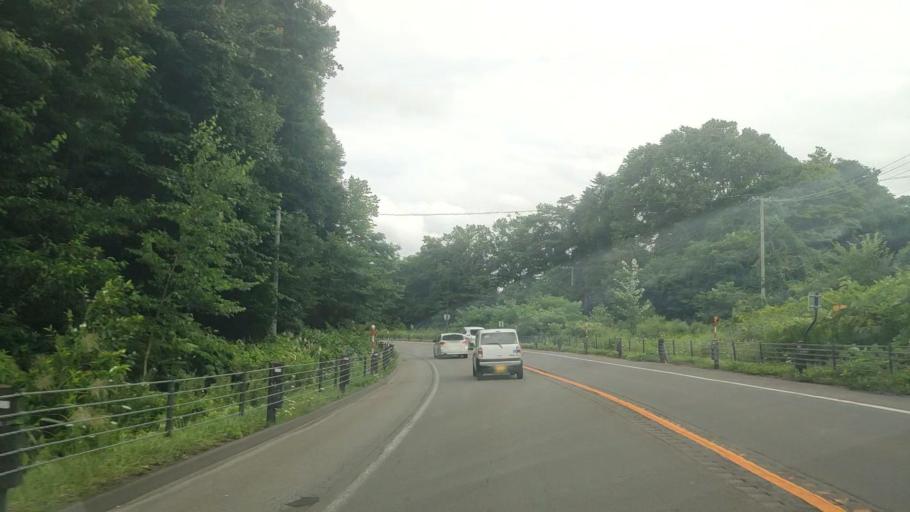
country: JP
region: Hokkaido
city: Nanae
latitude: 41.9689
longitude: 140.6509
